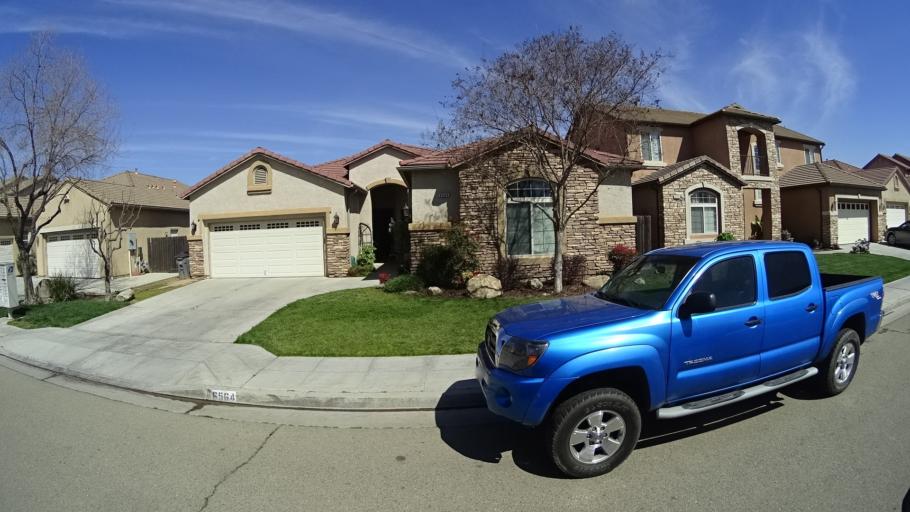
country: US
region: California
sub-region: Fresno County
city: Biola
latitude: 36.8176
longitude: -119.9089
